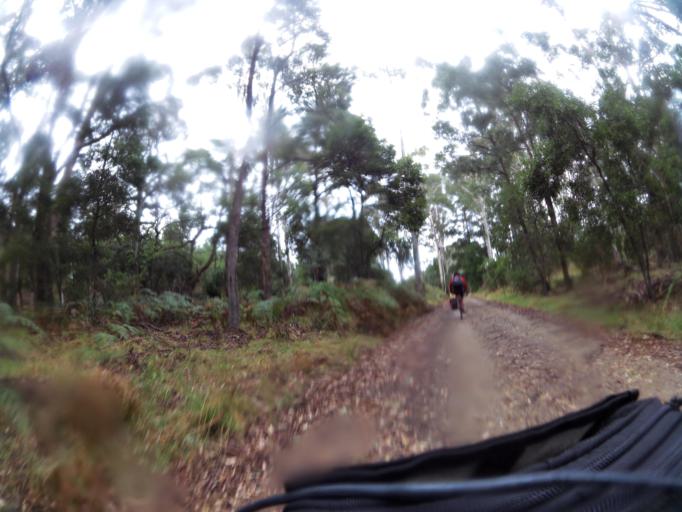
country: AU
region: New South Wales
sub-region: Greater Hume Shire
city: Holbrook
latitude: -36.1928
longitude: 147.5390
